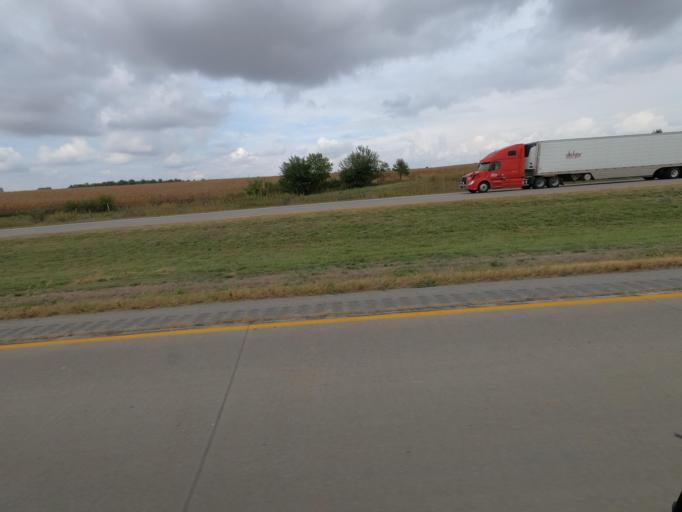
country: US
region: Iowa
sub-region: Jasper County
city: Prairie City
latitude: 41.5880
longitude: -93.2244
